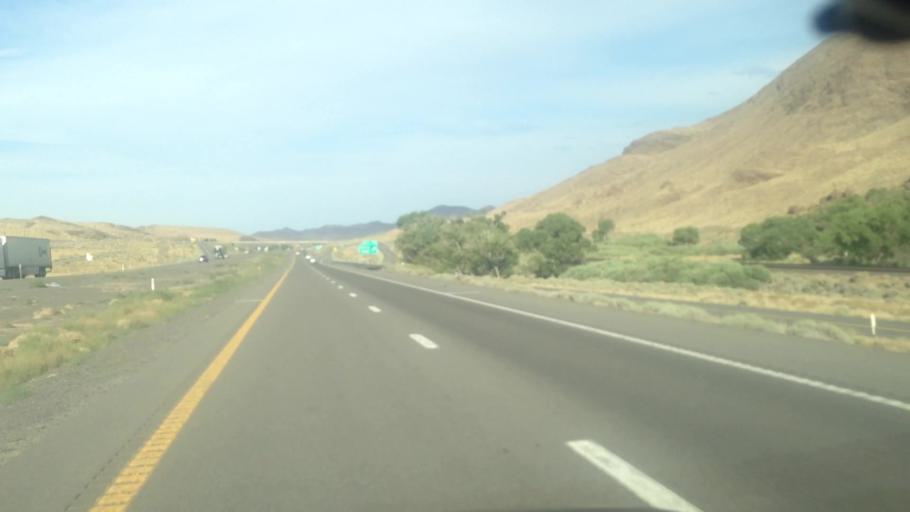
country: US
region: Nevada
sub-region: Lyon County
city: Fernley
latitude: 39.5891
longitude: -119.4368
